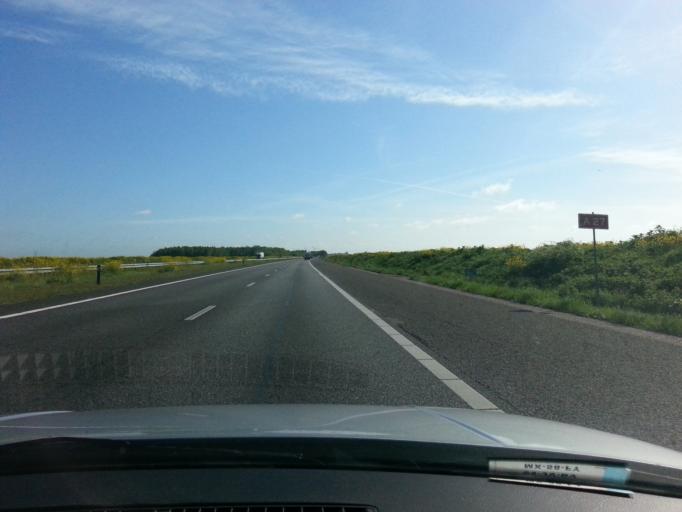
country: NL
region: North Holland
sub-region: Gemeente Huizen
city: Huizen
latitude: 52.2893
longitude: 5.2827
